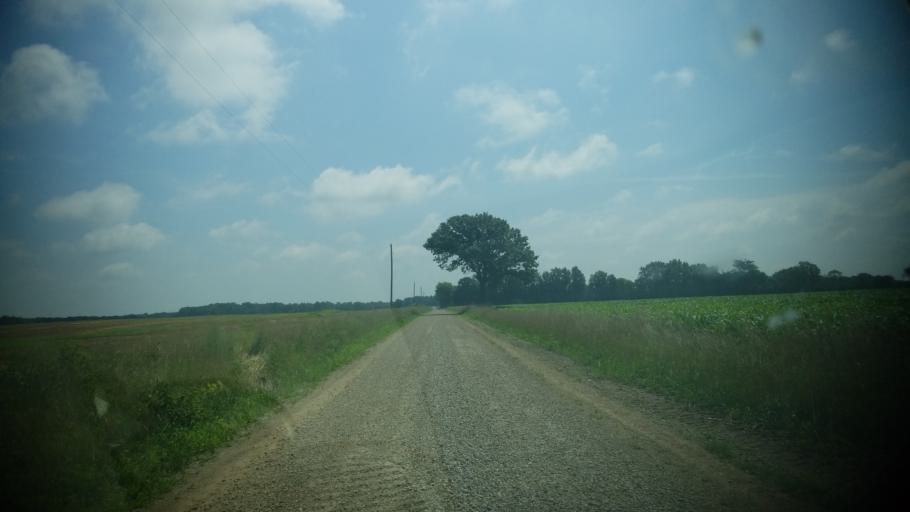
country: US
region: Illinois
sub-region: Wayne County
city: Fairfield
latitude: 38.5299
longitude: -88.3791
